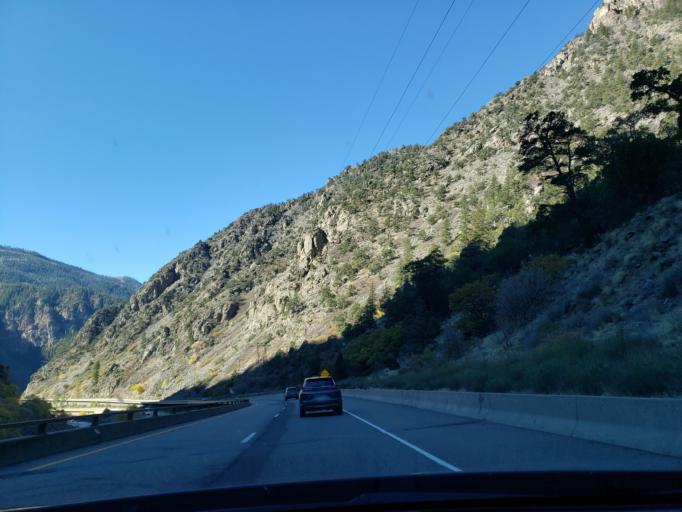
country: US
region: Colorado
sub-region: Garfield County
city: Glenwood Springs
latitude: 39.5667
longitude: -107.2326
